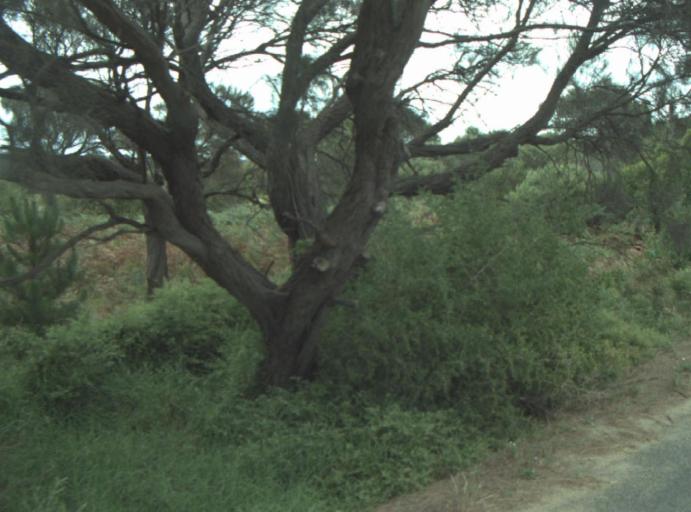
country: AU
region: Victoria
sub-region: Queenscliffe
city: Queenscliff
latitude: -38.2670
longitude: 144.5779
